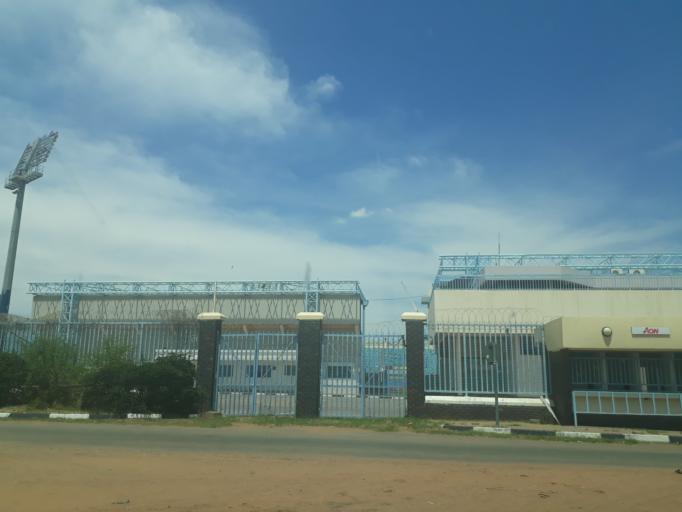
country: BW
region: South East
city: Gaborone
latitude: -24.6566
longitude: 25.9316
